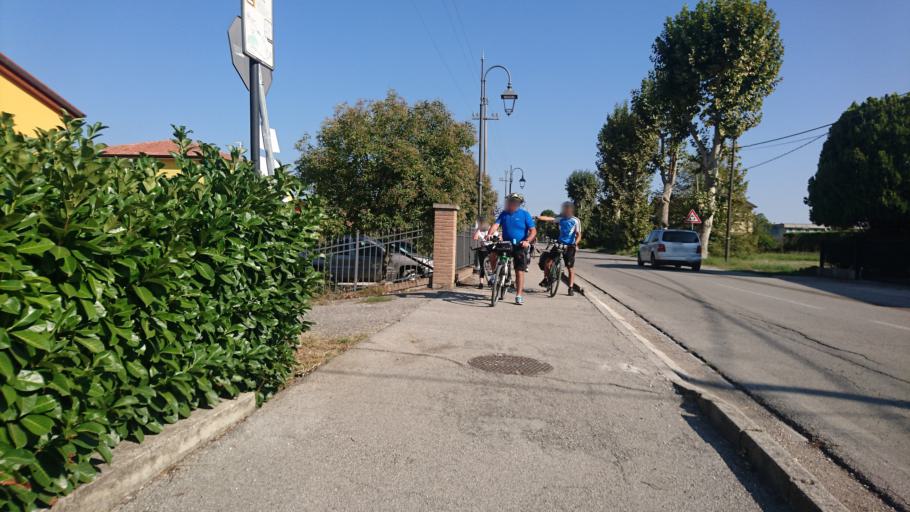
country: IT
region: Veneto
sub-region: Provincia di Padova
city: Galzignano
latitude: 45.2891
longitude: 11.7395
